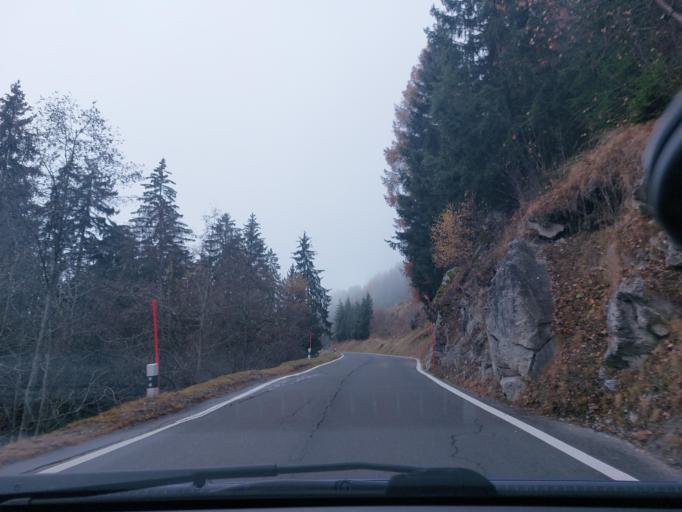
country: CH
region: Valais
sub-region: Conthey District
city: Basse-Nendaz
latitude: 46.1642
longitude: 7.3123
